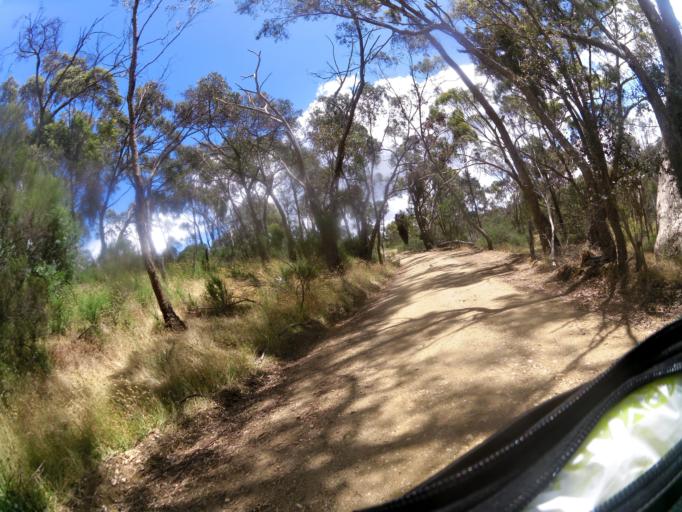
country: AU
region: Victoria
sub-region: Mount Alexander
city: Castlemaine
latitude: -37.0564
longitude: 144.2715
